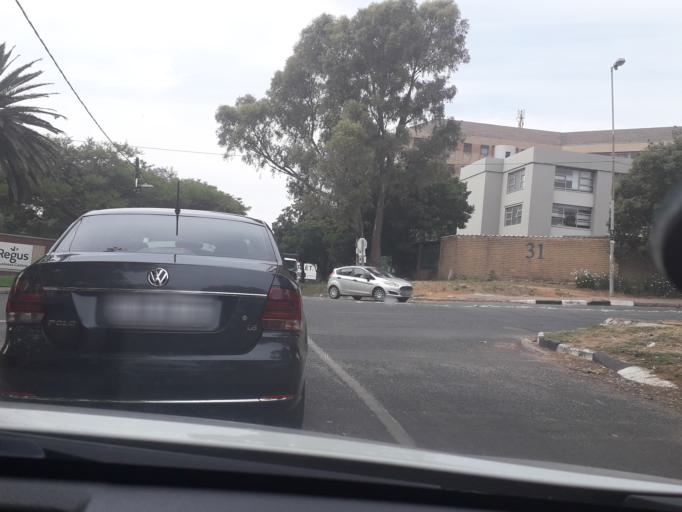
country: ZA
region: Gauteng
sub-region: City of Johannesburg Metropolitan Municipality
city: Johannesburg
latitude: -26.0962
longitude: 27.9979
